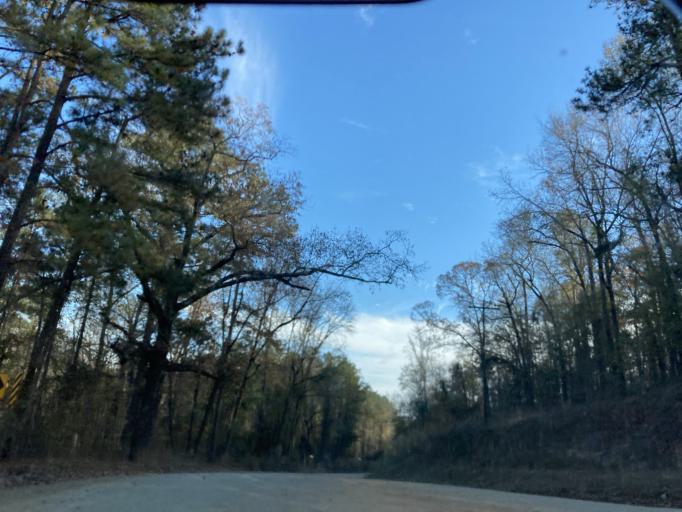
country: US
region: Georgia
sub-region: Jones County
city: Gray
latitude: 32.9121
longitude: -83.4895
